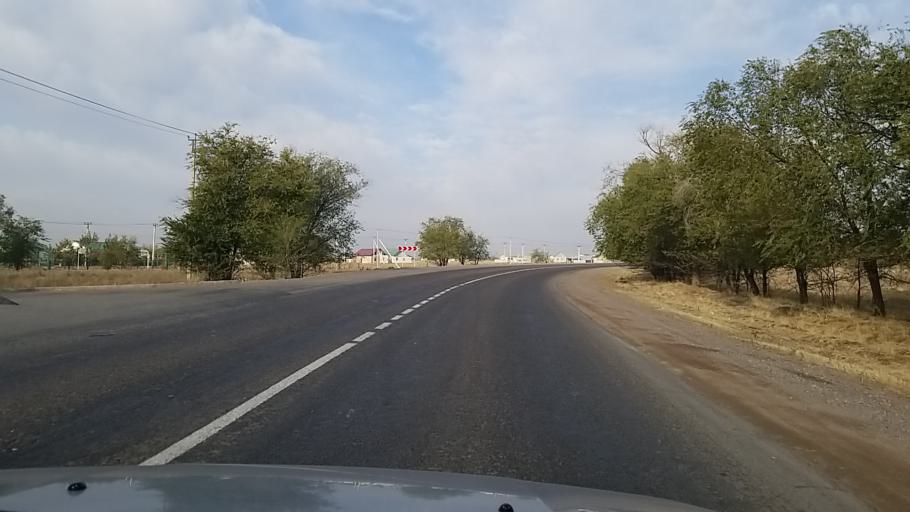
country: KZ
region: Almaty Oblysy
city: Burunday
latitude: 43.4777
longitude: 76.6817
